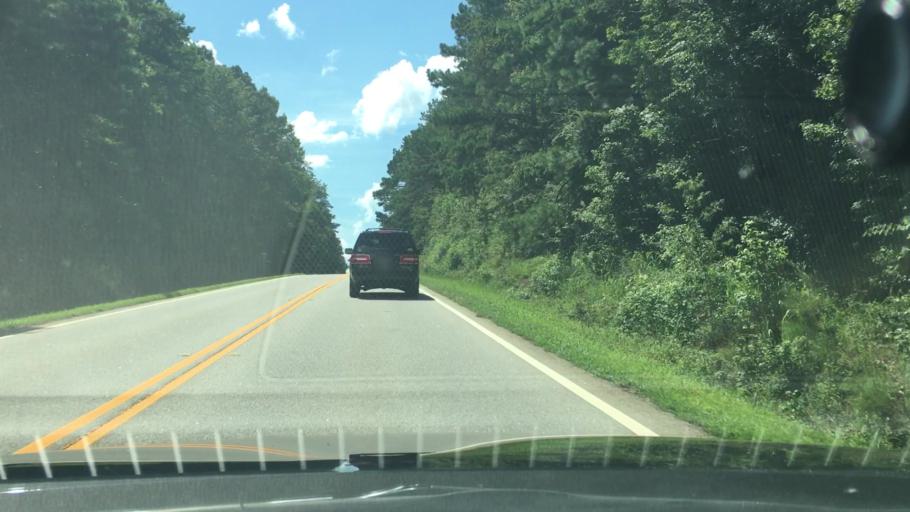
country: US
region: Georgia
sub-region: Putnam County
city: Eatonton
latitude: 33.3108
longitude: -83.5260
